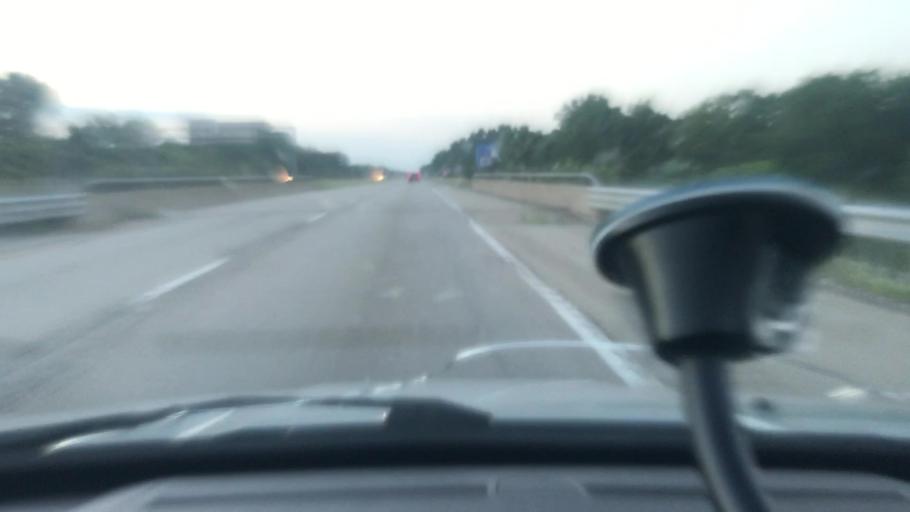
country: US
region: Illinois
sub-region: Peoria County
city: Bellevue
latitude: 40.7541
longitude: -89.6710
